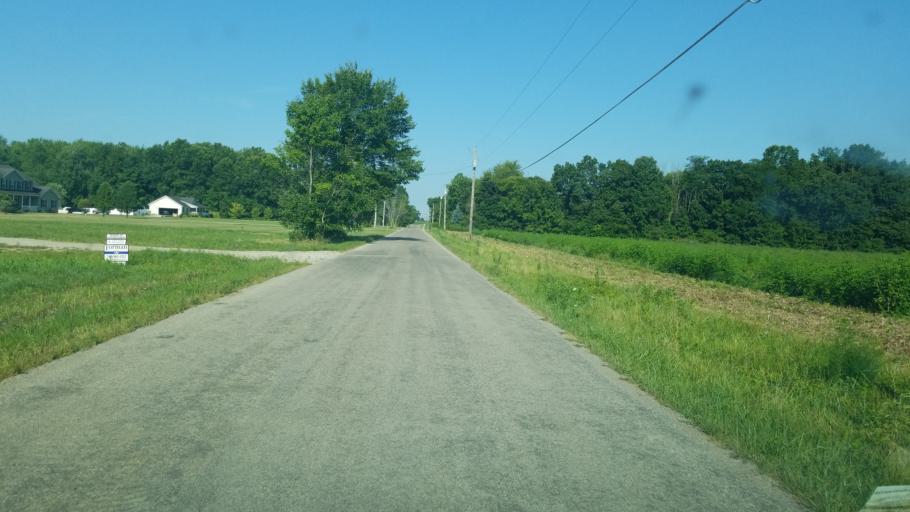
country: US
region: Ohio
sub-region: Knox County
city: Centerburg
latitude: 40.3816
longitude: -82.7826
